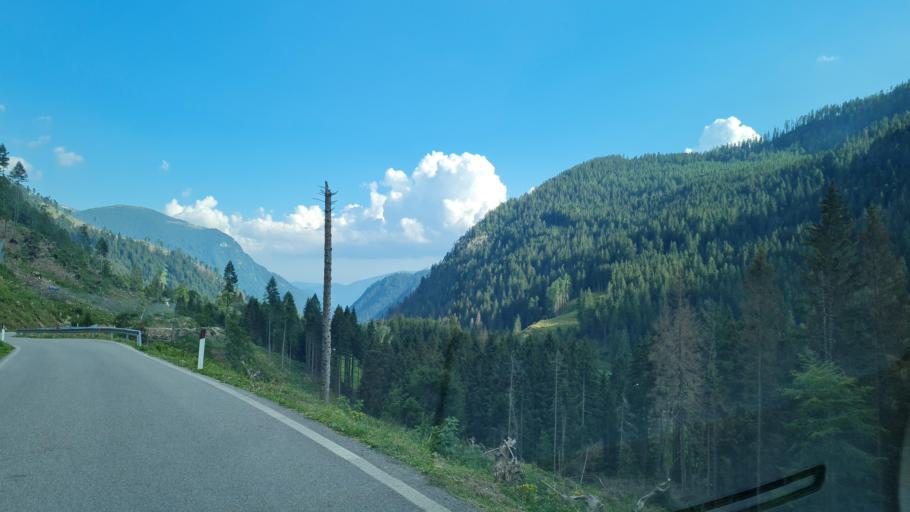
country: IT
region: Trentino-Alto Adige
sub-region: Provincia di Trento
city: Torcegno
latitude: 46.1446
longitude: 11.4637
